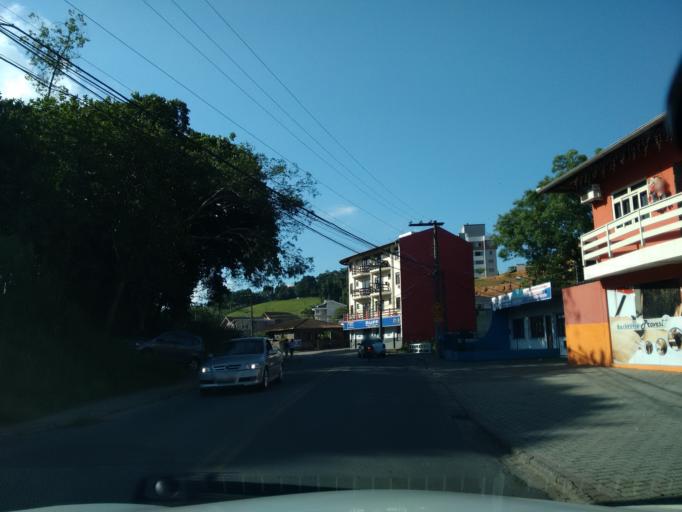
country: BR
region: Santa Catarina
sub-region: Blumenau
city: Blumenau
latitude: -26.8759
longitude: -49.0664
